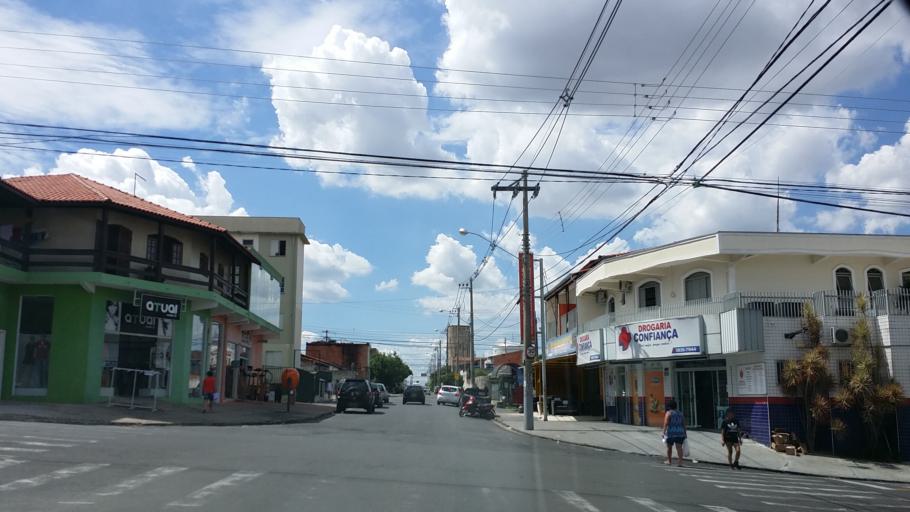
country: BR
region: Sao Paulo
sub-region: Indaiatuba
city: Indaiatuba
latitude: -23.1194
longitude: -47.2418
